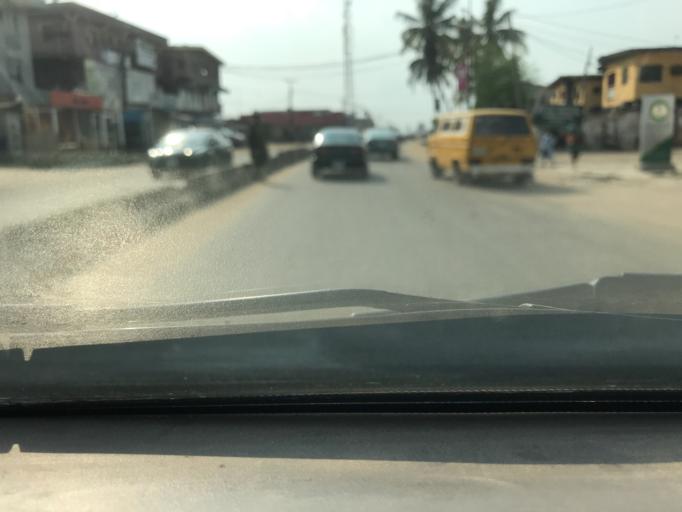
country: NG
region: Lagos
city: Agege
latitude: 6.6024
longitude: 3.3090
